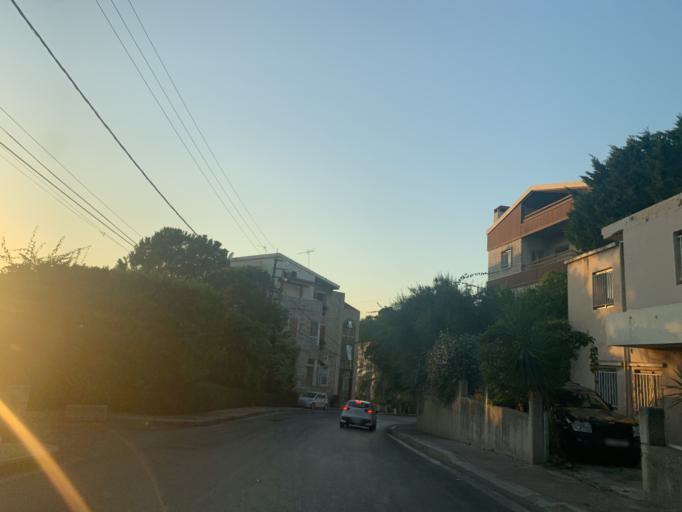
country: LB
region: Mont-Liban
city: Djounie
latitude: 33.9598
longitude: 35.6336
